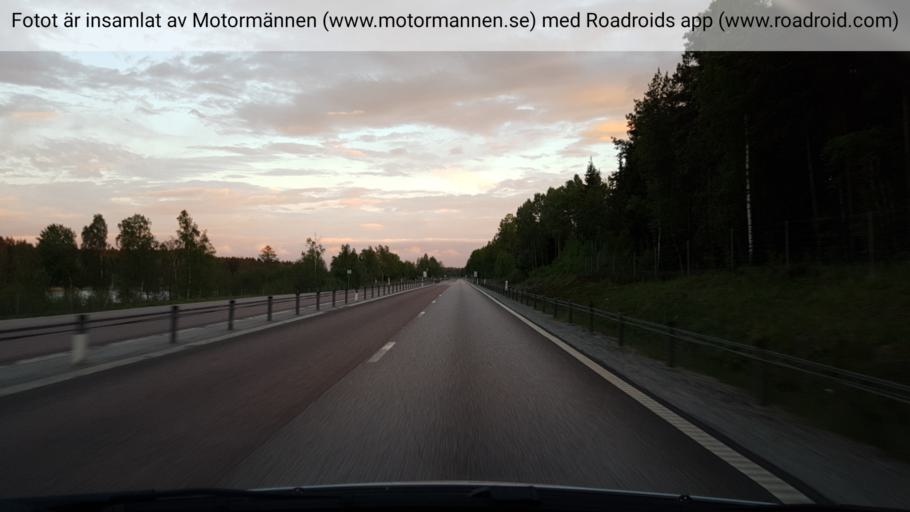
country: SE
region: Vaestmanland
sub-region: Surahammars Kommun
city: Ramnas
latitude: 59.7937
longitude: 16.1469
